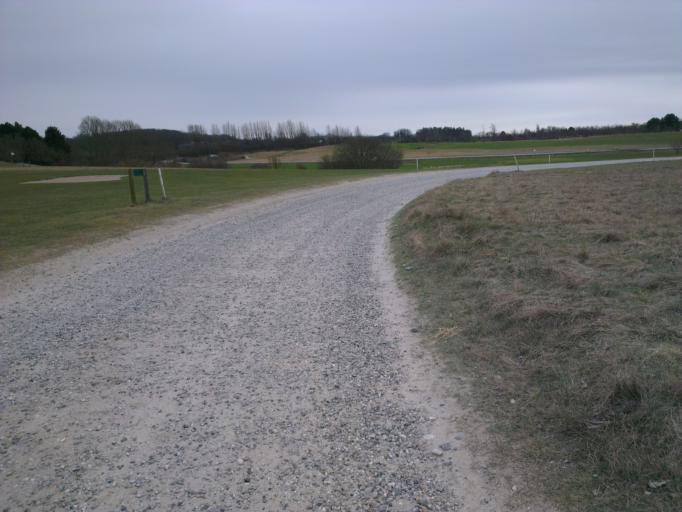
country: DK
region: Capital Region
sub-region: Frederikssund Kommune
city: Frederikssund
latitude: 55.8365
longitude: 12.0236
